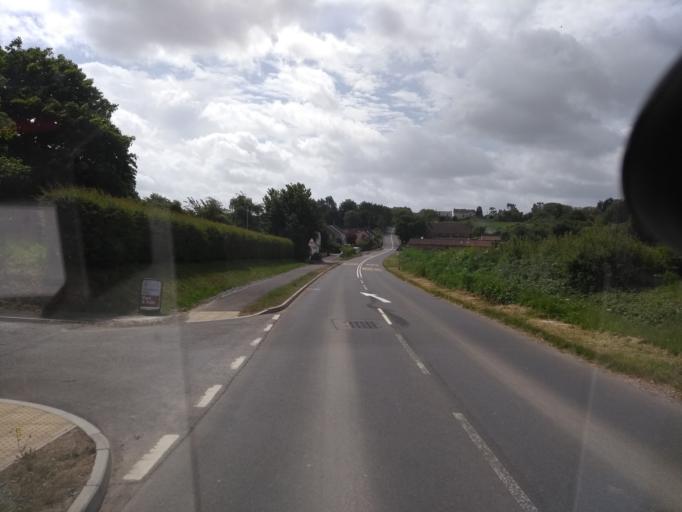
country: GB
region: England
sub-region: Somerset
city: Bridgwater
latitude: 51.1584
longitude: -3.0653
